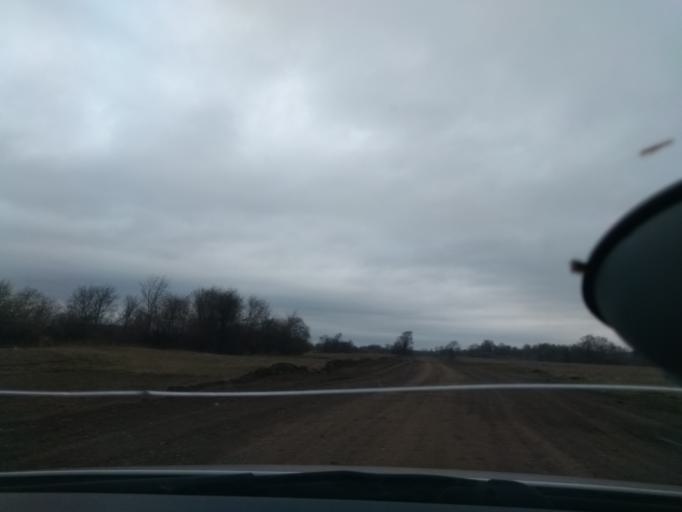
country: RU
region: Perm
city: Orda
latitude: 57.2345
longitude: 56.6104
